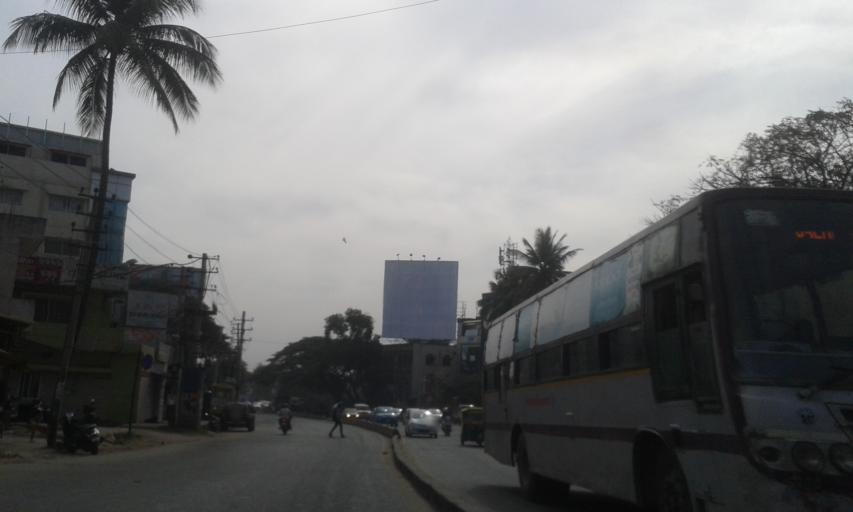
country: IN
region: Karnataka
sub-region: Bangalore Urban
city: Bangalore
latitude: 12.9248
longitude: 77.6379
